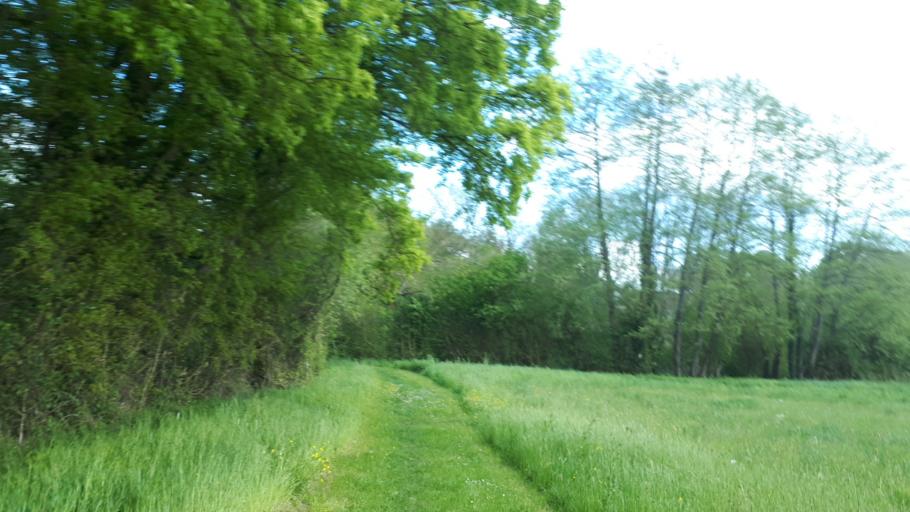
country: FR
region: Centre
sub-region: Departement du Loir-et-Cher
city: Aze
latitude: 47.8485
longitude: 0.9980
